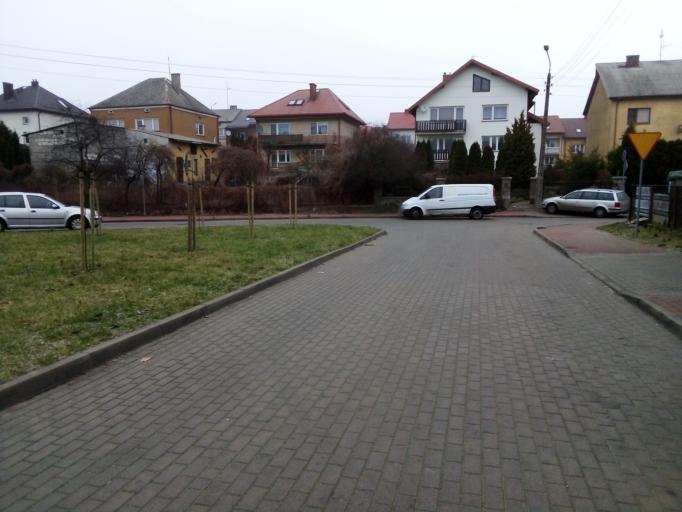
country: PL
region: Podlasie
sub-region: Powiat kolnenski
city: Kolno
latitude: 53.4144
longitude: 21.9352
